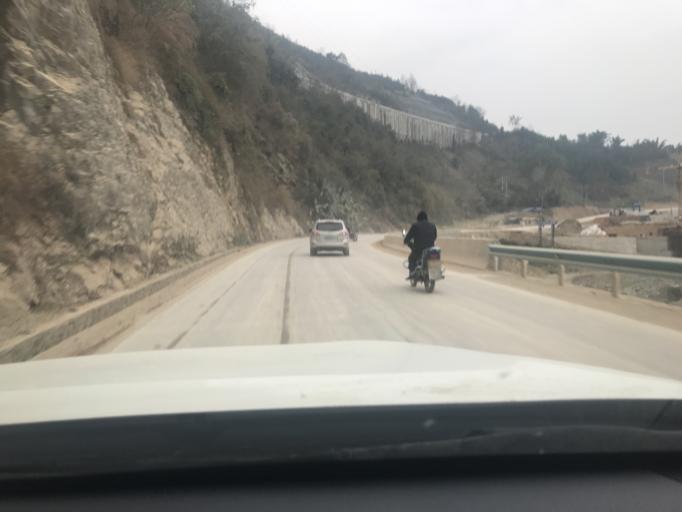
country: CN
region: Guangxi Zhuangzu Zizhiqu
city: Xinzhou
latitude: 25.0099
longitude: 105.8544
